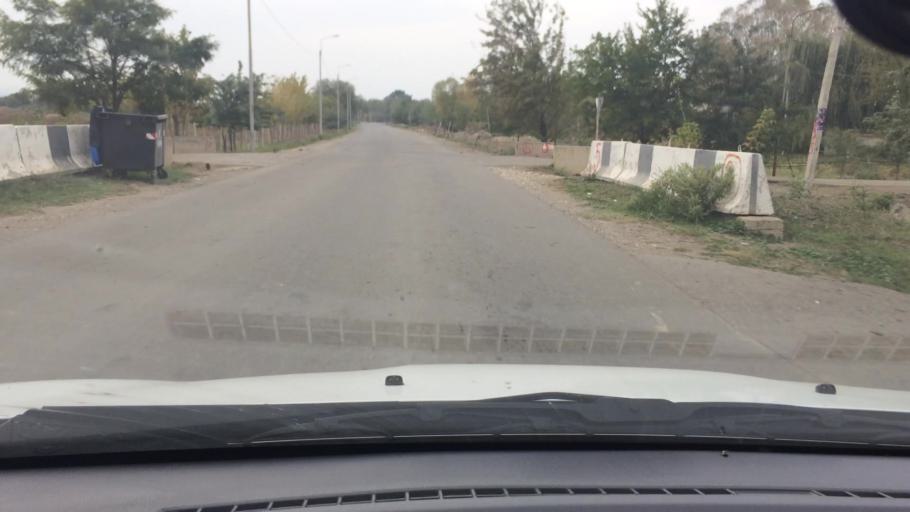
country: AM
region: Tavush
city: Berdavan
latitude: 41.3481
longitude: 44.9771
